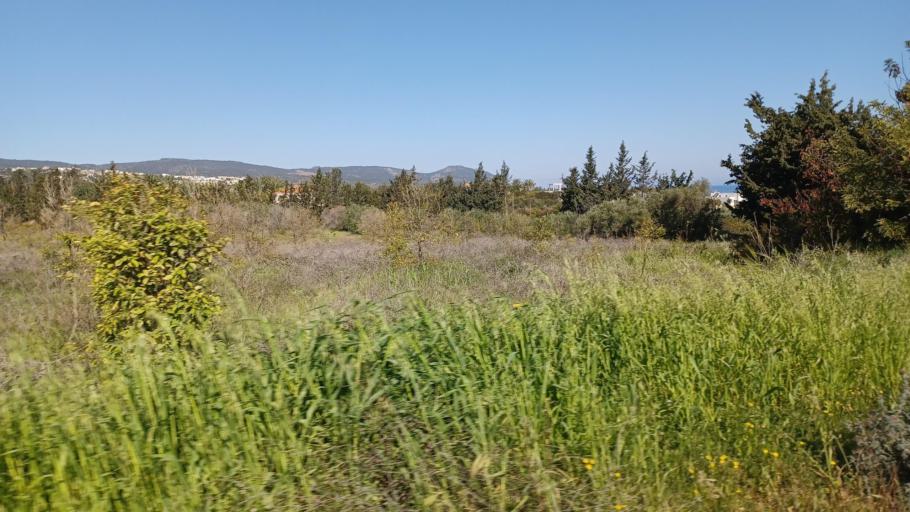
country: CY
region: Pafos
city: Polis
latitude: 35.0268
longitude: 32.3931
